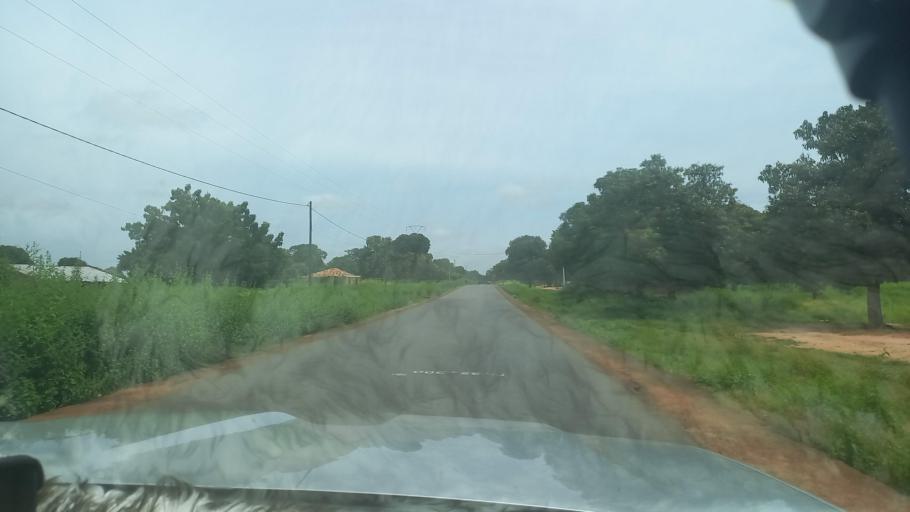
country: SN
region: Kolda
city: Marsassoum
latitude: 12.9631
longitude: -15.9795
